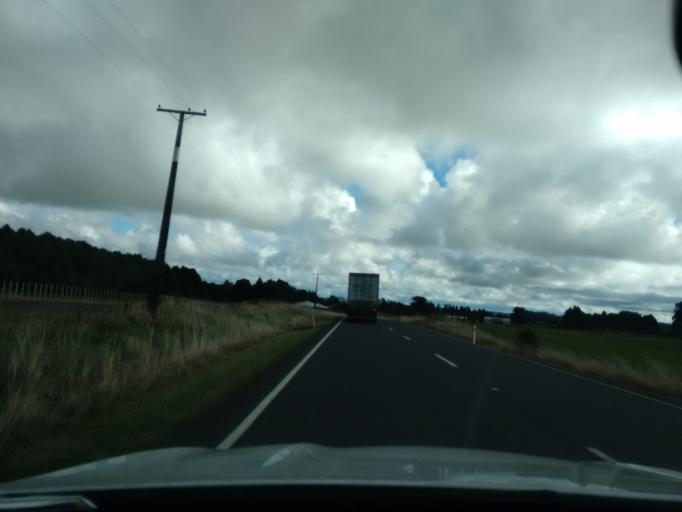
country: NZ
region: Manawatu-Wanganui
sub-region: Ruapehu District
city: Waiouru
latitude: -39.3575
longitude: 175.3514
